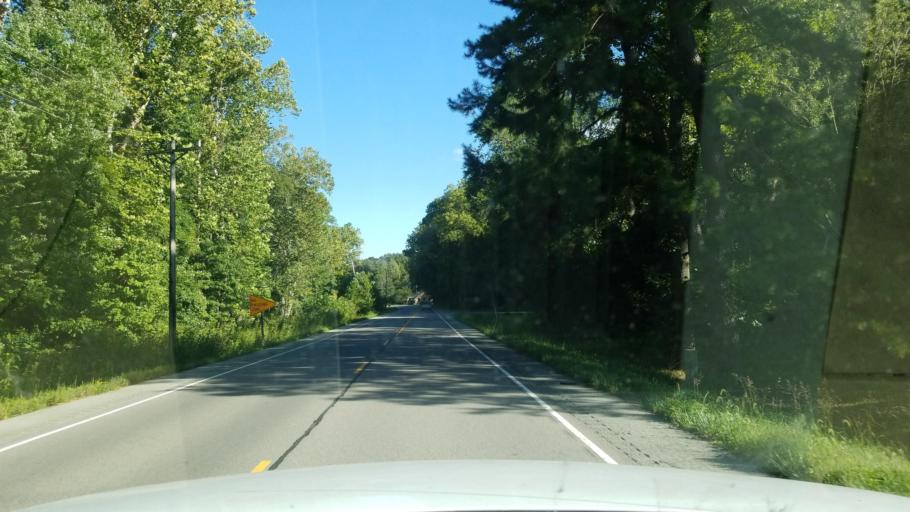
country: US
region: Illinois
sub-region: Saline County
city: Harrisburg
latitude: 37.5842
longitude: -88.4424
